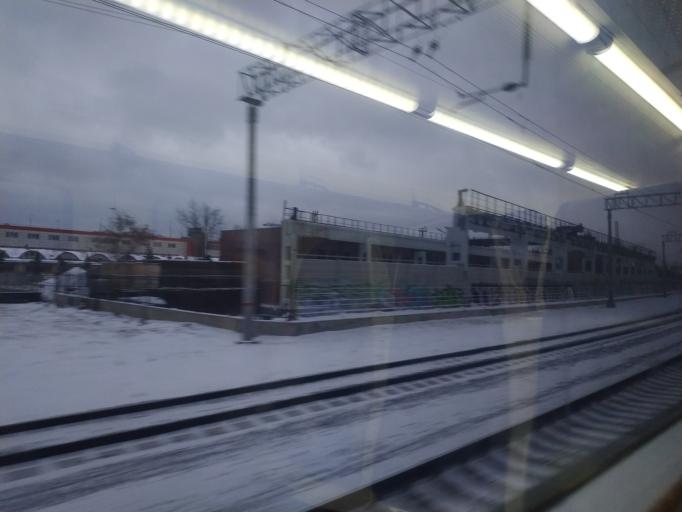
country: RU
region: Moscow
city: Taganskiy
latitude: 55.7406
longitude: 37.6924
